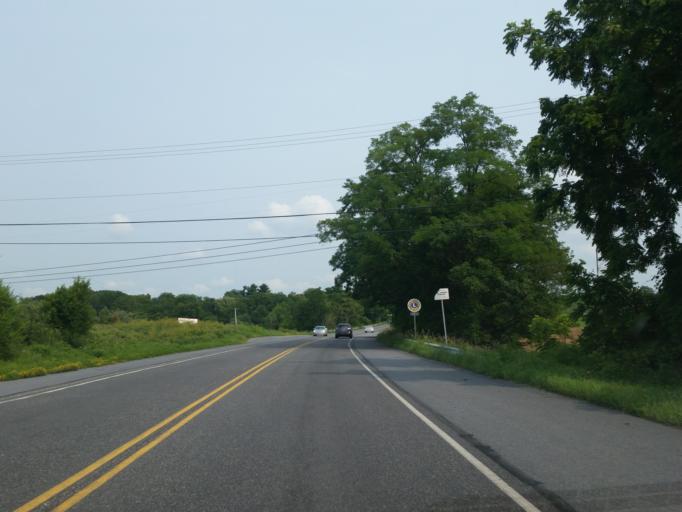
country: US
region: Pennsylvania
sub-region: Dauphin County
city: Skyline View
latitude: 40.3778
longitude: -76.6567
